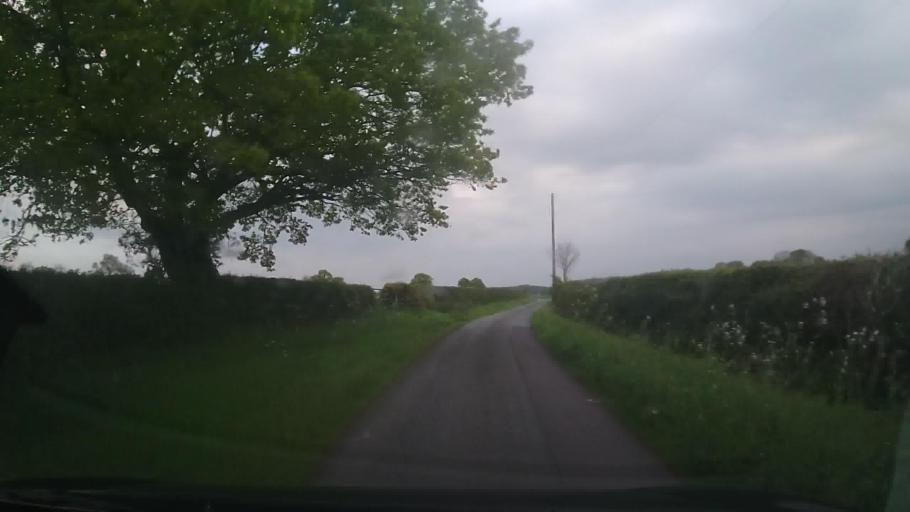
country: GB
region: England
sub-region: Shropshire
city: Ellesmere
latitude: 52.9363
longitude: -2.8609
